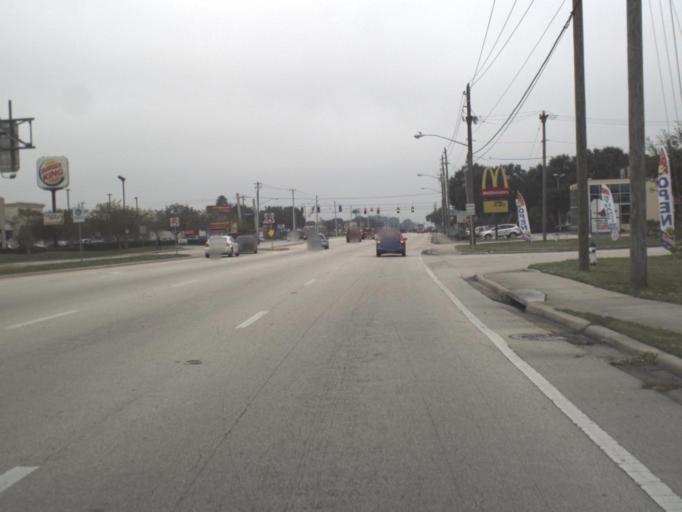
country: US
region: Florida
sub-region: Brevard County
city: Palm Bay
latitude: 27.9987
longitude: -80.6322
